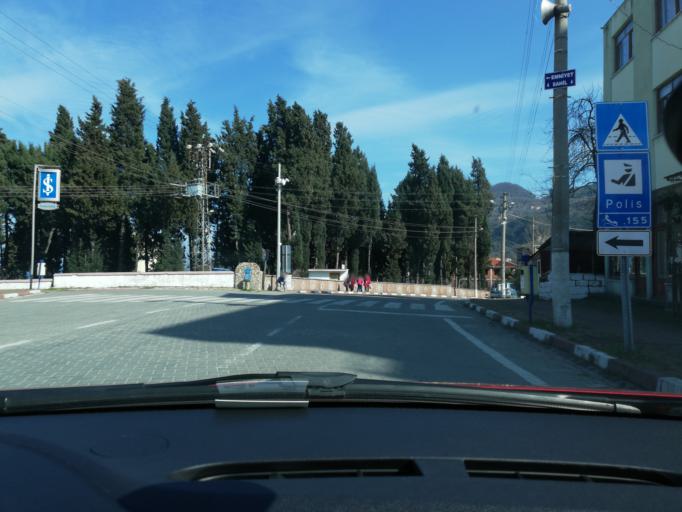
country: TR
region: Bartin
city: Kurucasile
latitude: 41.8456
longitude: 32.7176
